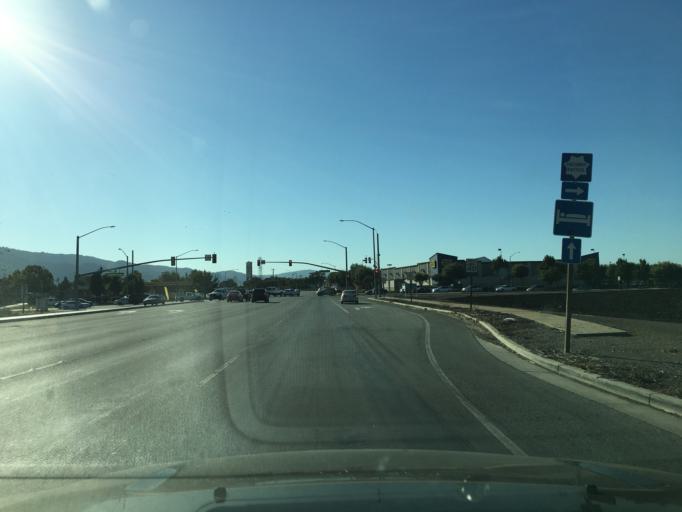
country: US
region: California
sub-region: Santa Clara County
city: Gilroy
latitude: 37.0042
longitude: -121.5494
